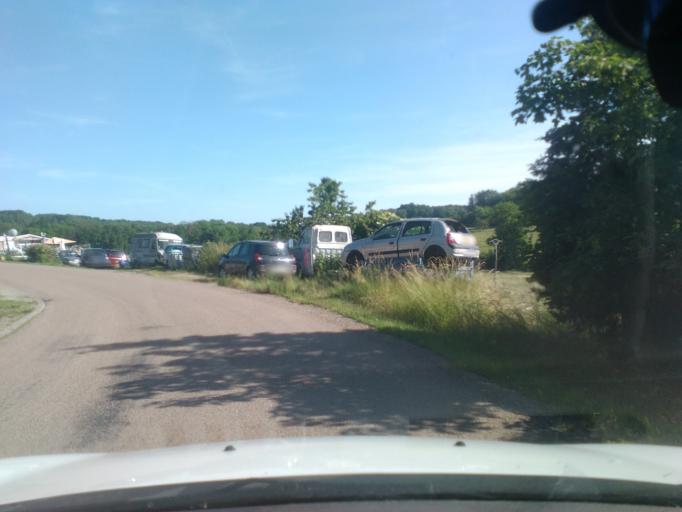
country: FR
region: Lorraine
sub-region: Departement des Vosges
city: Mirecourt
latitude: 48.3393
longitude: 6.1931
